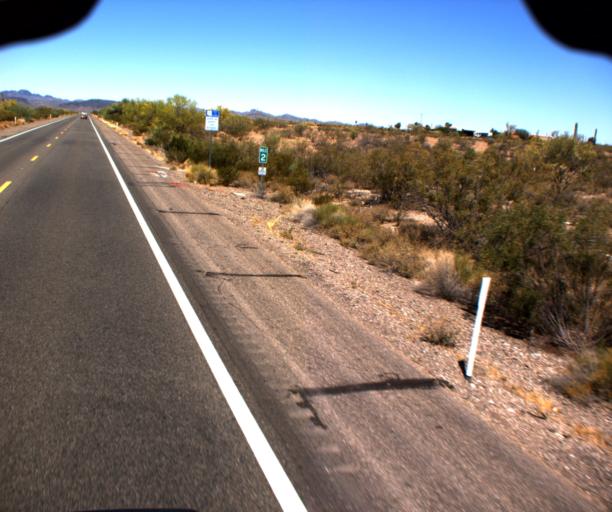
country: US
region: Arizona
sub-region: Maricopa County
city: Wickenburg
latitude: 33.8599
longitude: -112.6008
